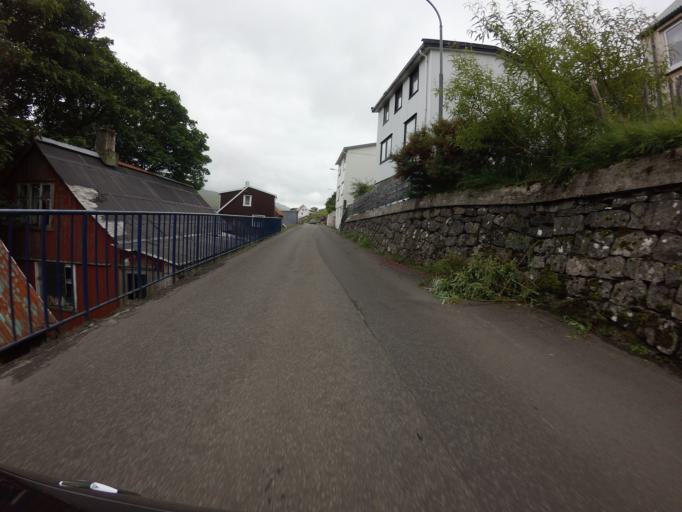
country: FO
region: Eysturoy
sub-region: Eidi
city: Eidi
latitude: 62.2734
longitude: -7.0920
